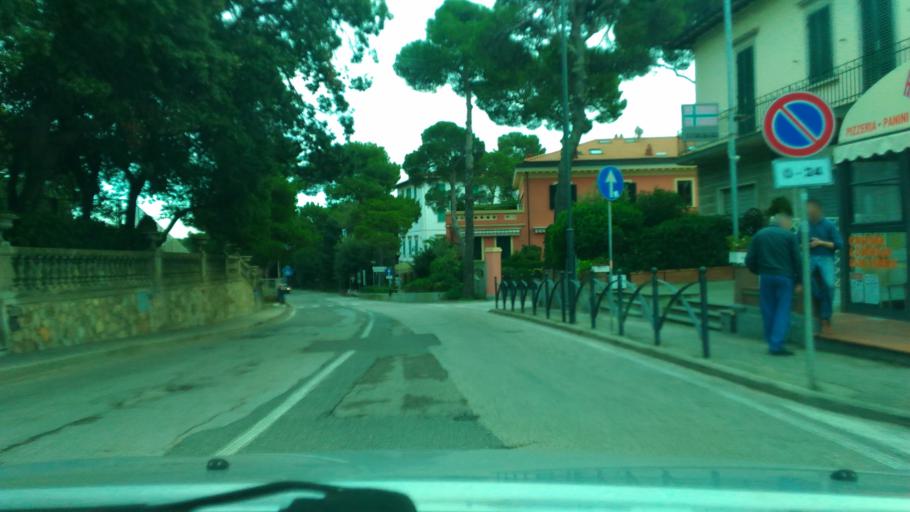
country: IT
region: Tuscany
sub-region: Provincia di Livorno
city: Rosignano Solvay-Castiglioncello
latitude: 43.4053
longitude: 10.4104
